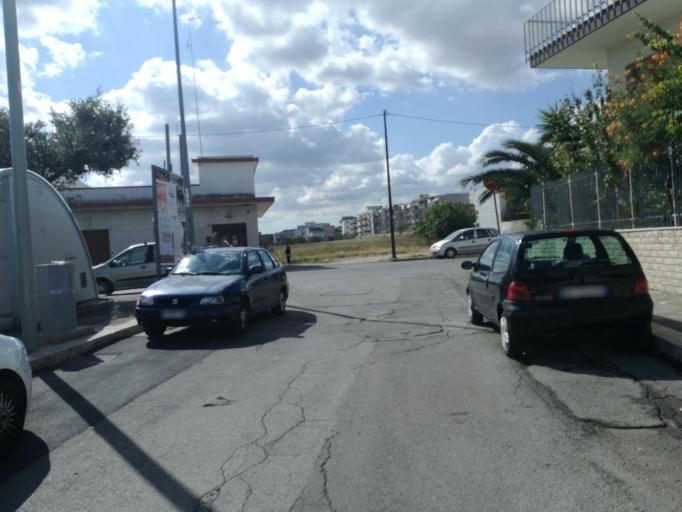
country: IT
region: Apulia
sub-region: Provincia di Bari
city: Triggiano
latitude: 41.0640
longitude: 16.9301
